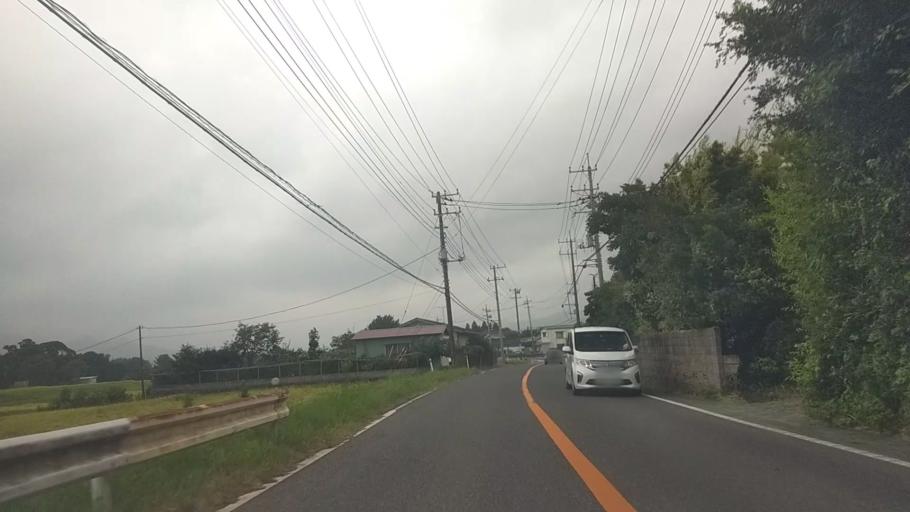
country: JP
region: Chiba
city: Kawaguchi
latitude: 35.1267
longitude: 140.0557
